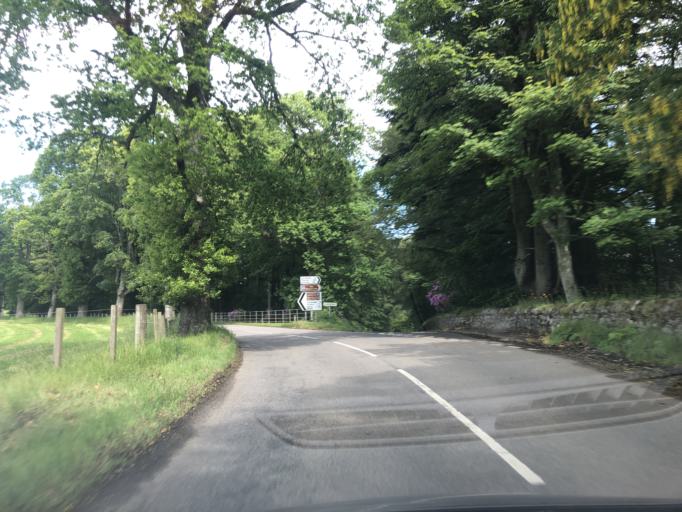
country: GB
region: Scotland
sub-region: Angus
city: Kirriemuir
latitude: 56.7225
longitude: -2.9949
